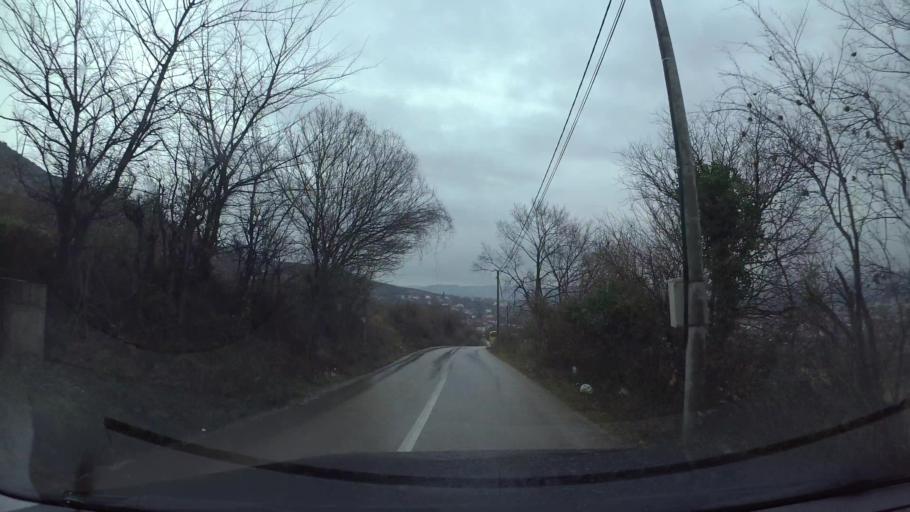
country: BA
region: Federation of Bosnia and Herzegovina
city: Blagaj
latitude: 43.2934
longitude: 17.8578
